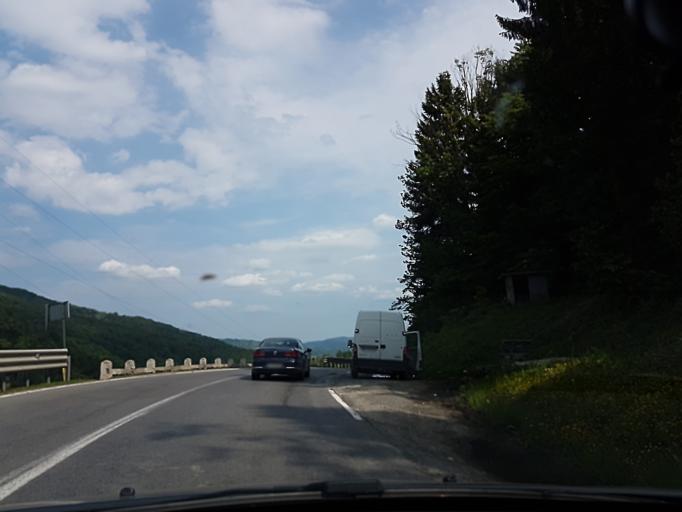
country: RO
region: Prahova
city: Maneciu
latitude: 45.3448
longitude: 25.9485
